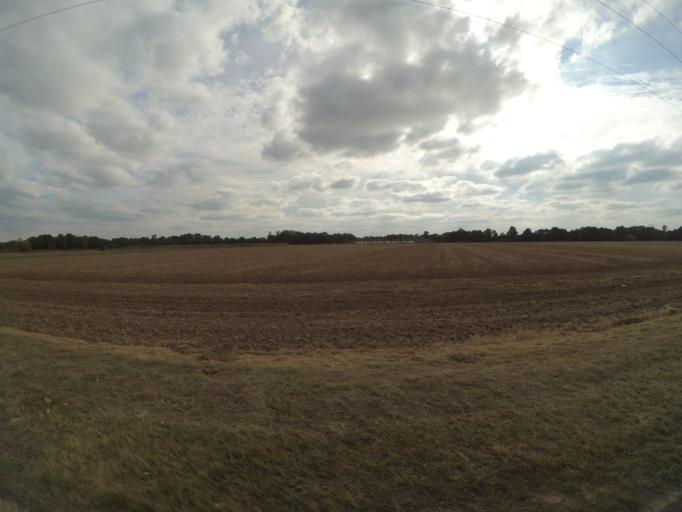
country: FR
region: Centre
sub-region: Departement d'Indre-et-Loire
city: Vouvray
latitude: 47.4043
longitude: 0.8183
